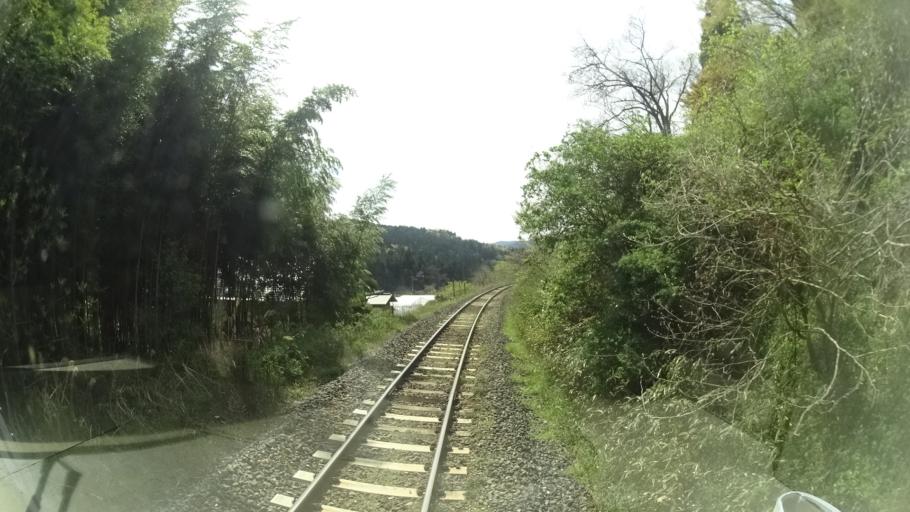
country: JP
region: Iwate
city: Ofunato
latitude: 38.9338
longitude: 141.4656
